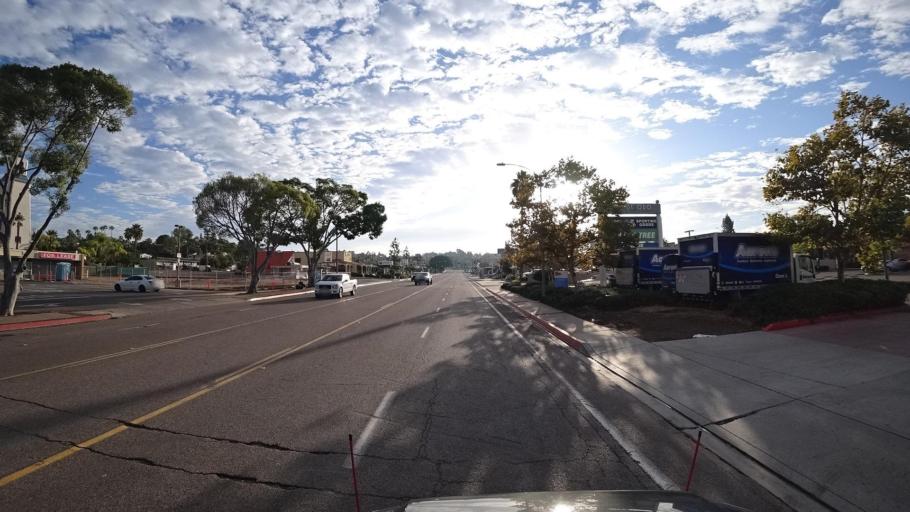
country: US
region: California
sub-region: San Diego County
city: Spring Valley
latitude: 32.7480
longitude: -116.9854
